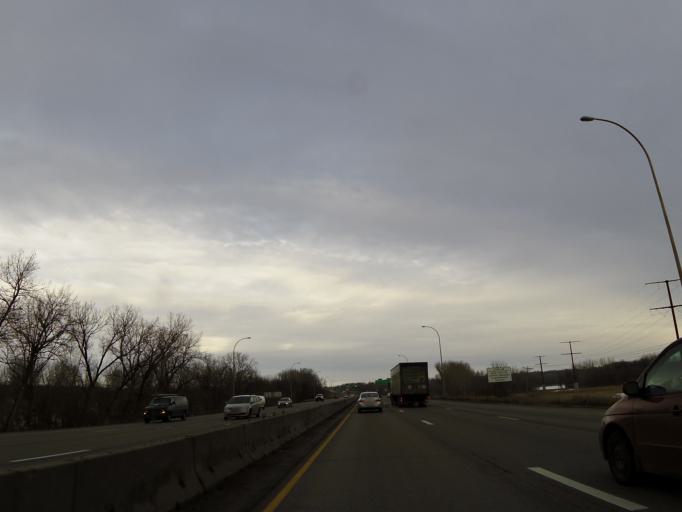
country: US
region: Minnesota
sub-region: Dakota County
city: Burnsville
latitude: 44.7910
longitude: -93.2893
